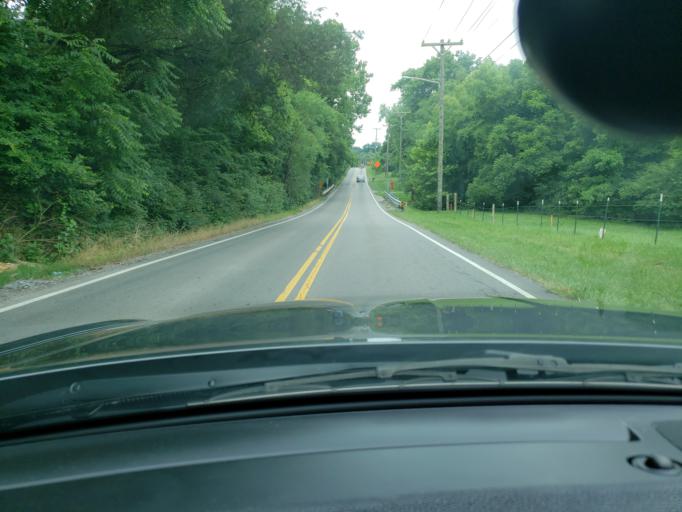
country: US
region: Tennessee
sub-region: Williamson County
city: Nolensville
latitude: 36.0250
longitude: -86.6802
